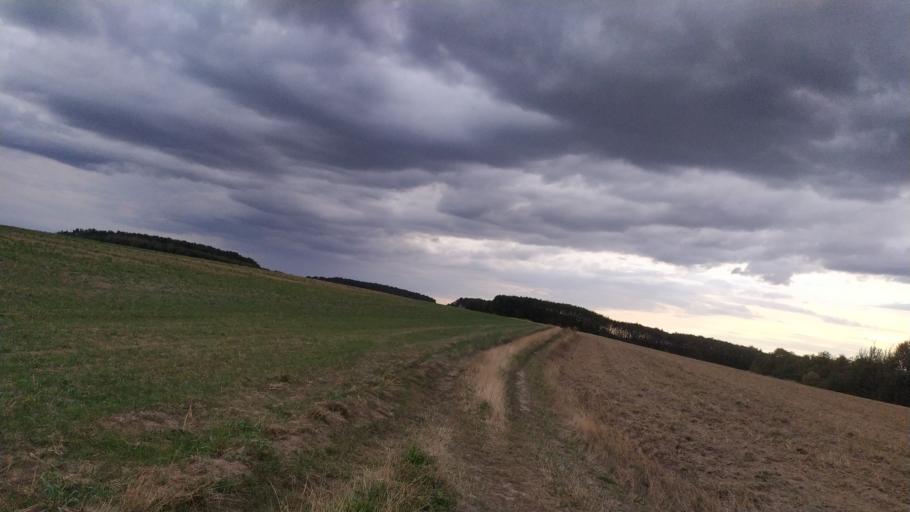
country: DE
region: Mecklenburg-Vorpommern
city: Wolgast
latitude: 54.0504
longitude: 13.8138
